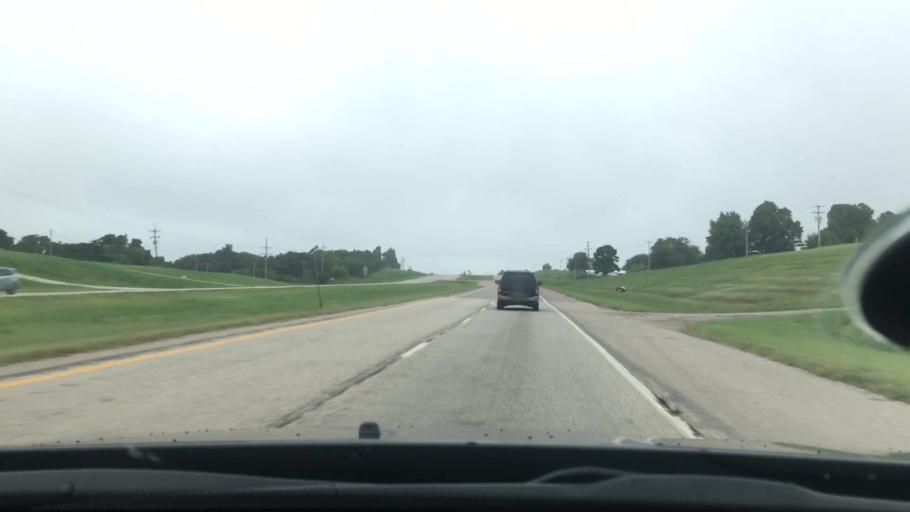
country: US
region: Oklahoma
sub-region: Seminole County
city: Seminole
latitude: 35.3017
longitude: -96.6707
